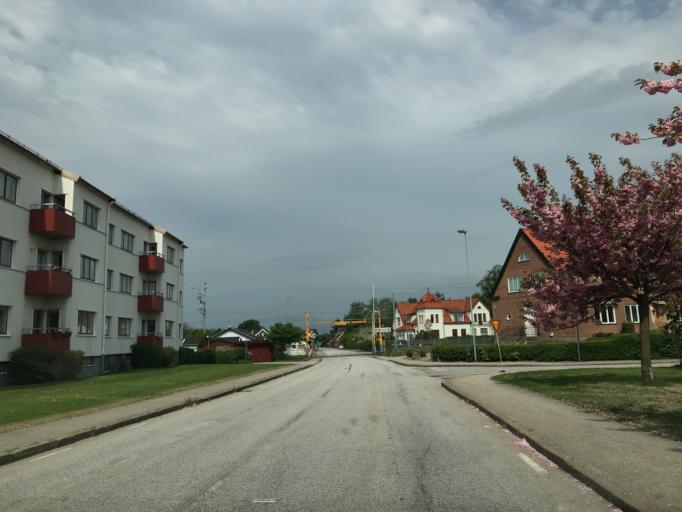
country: SE
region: Skane
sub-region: Svalovs Kommun
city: Svaloev
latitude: 55.8642
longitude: 13.1509
